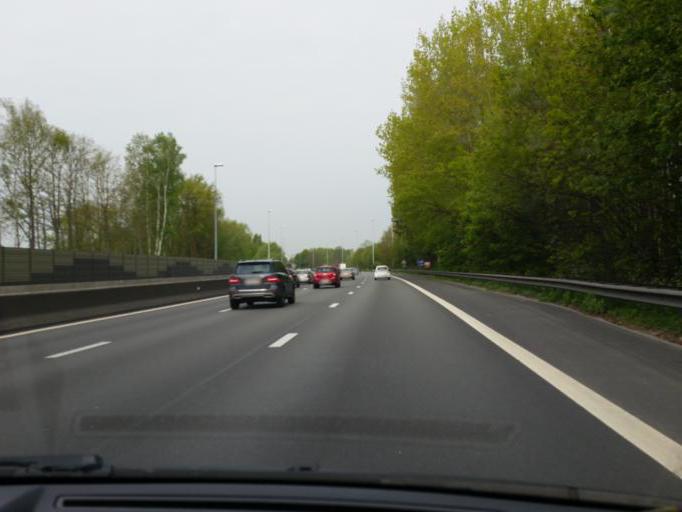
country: BE
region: Flanders
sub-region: Provincie Oost-Vlaanderen
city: Aalst
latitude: 50.9277
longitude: 4.0130
